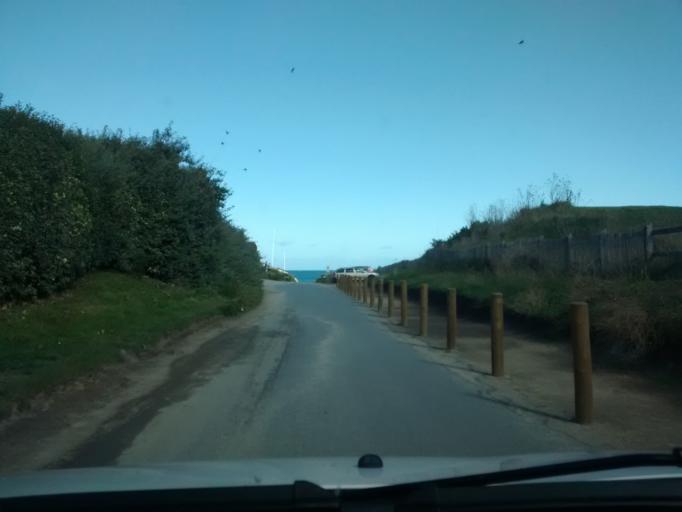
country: FR
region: Brittany
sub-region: Departement d'Ille-et-Vilaine
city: Saint-Briac-sur-Mer
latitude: 48.6306
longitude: -2.1422
